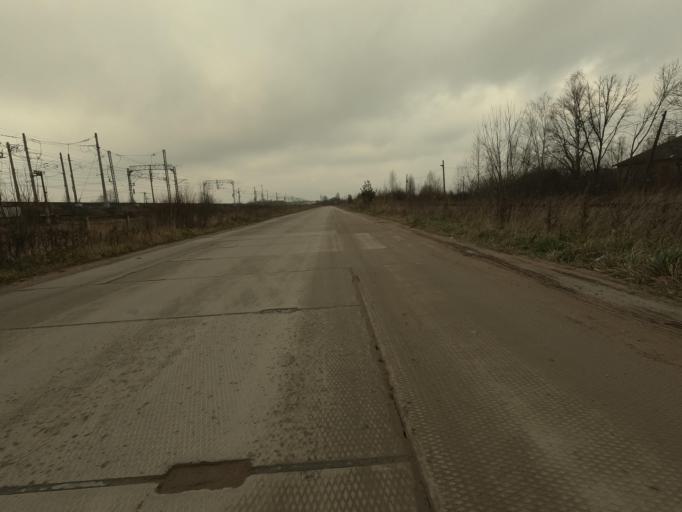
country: RU
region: Leningrad
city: Lyuban'
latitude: 59.4763
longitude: 31.2568
